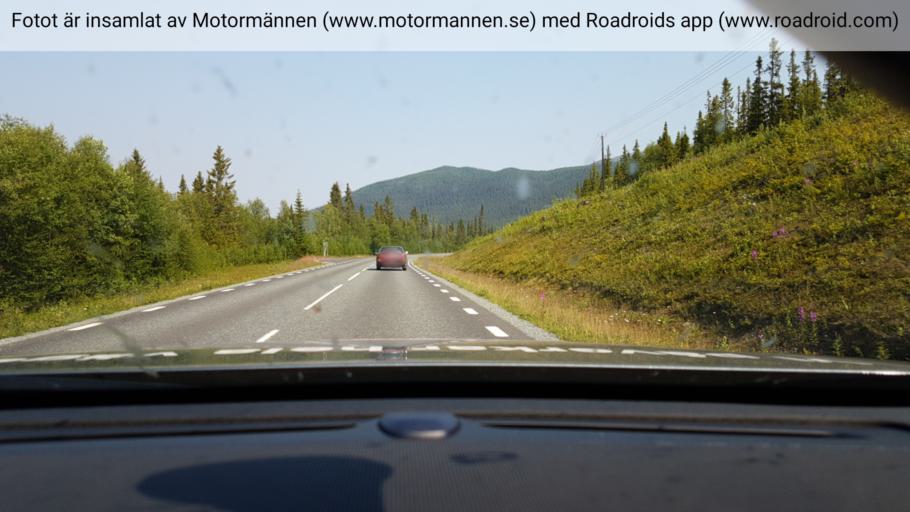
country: SE
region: Vaesterbotten
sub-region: Vilhelmina Kommun
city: Sjoberg
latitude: 65.6190
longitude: 15.5352
